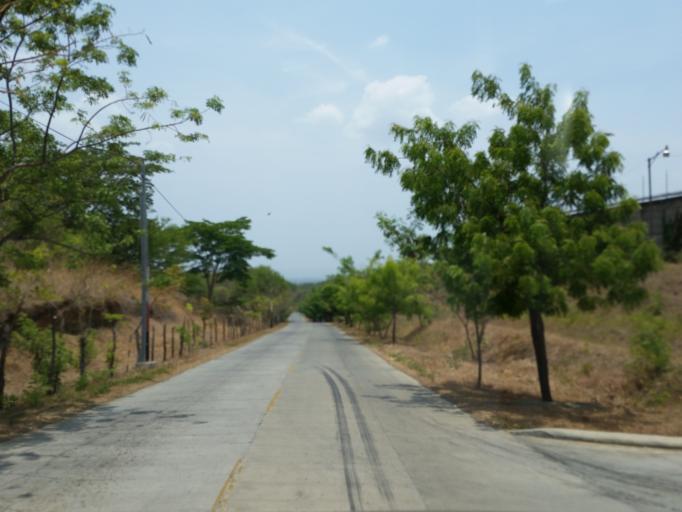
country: NI
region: Managua
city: Managua
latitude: 12.0769
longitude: -86.2456
